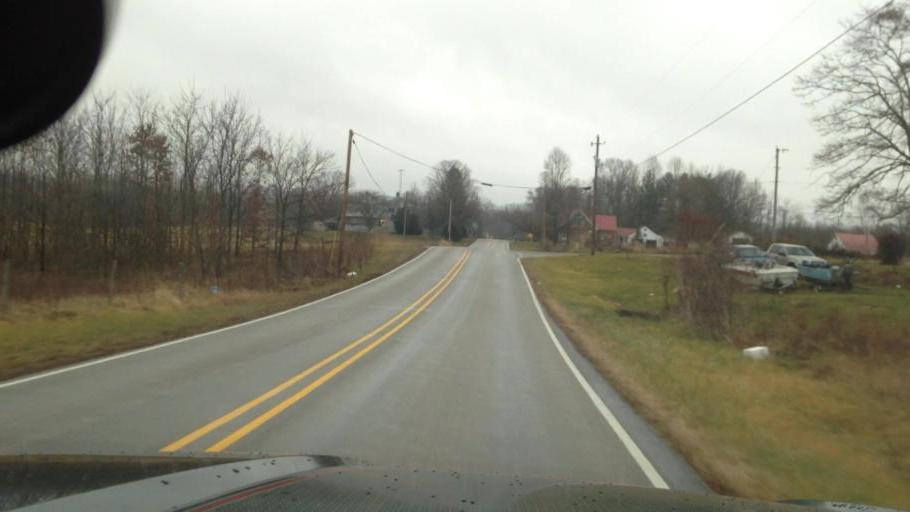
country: US
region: Ohio
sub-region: Preble County
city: New Paris
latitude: 39.8998
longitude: -84.8319
